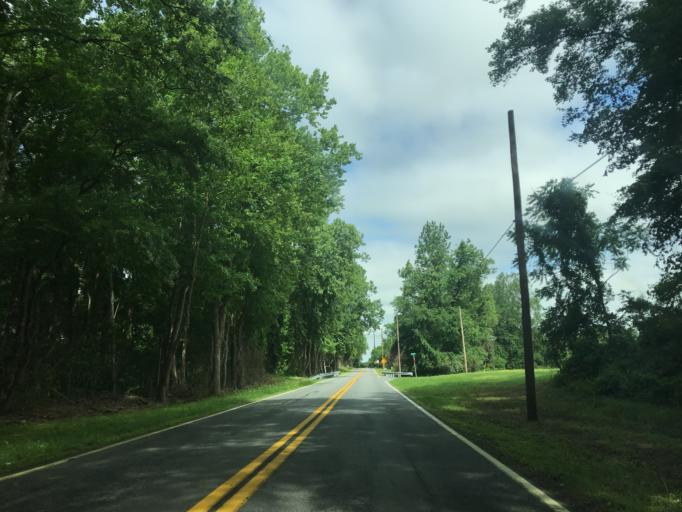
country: US
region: Maryland
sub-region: Caroline County
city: Ridgely
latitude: 38.8862
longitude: -75.9817
